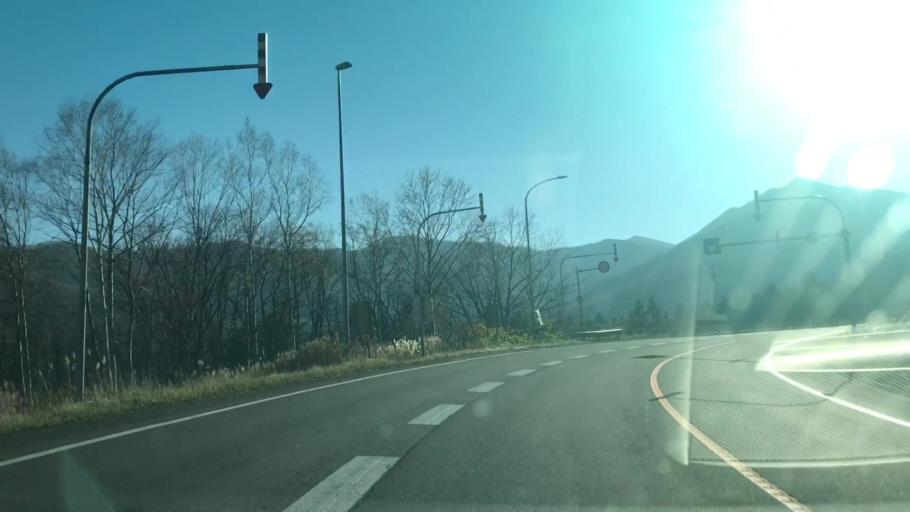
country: JP
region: Hokkaido
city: Otofuke
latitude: 42.9694
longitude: 142.8049
